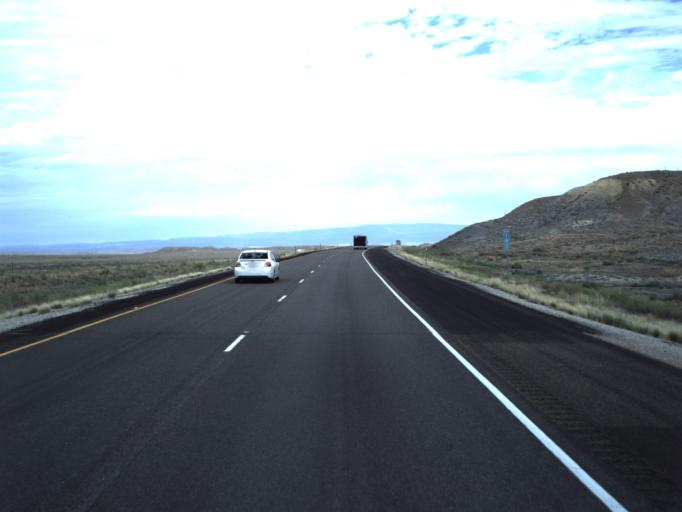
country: US
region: Utah
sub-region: Grand County
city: Moab
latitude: 38.9498
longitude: -109.6790
